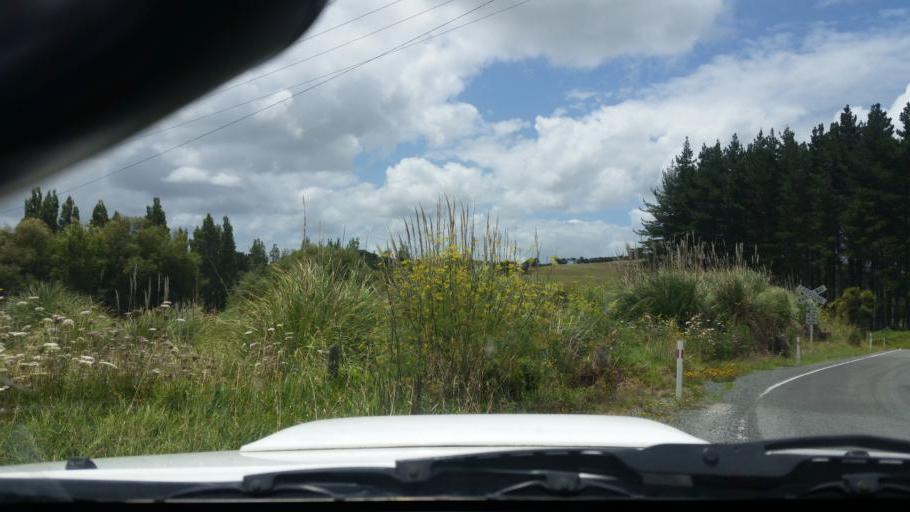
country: NZ
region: Auckland
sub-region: Auckland
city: Wellsford
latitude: -36.1234
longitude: 174.3317
